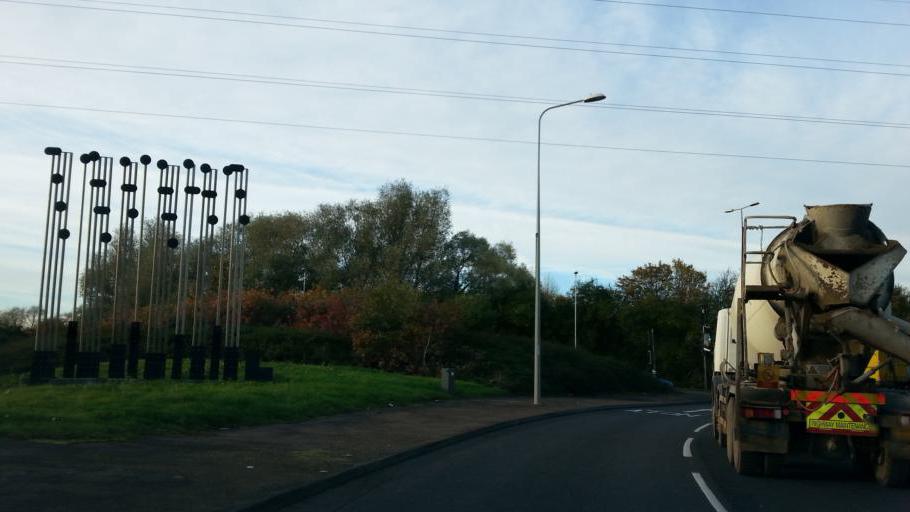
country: GB
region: England
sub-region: Northamptonshire
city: Hardingstone
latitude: 52.2306
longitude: -0.8712
